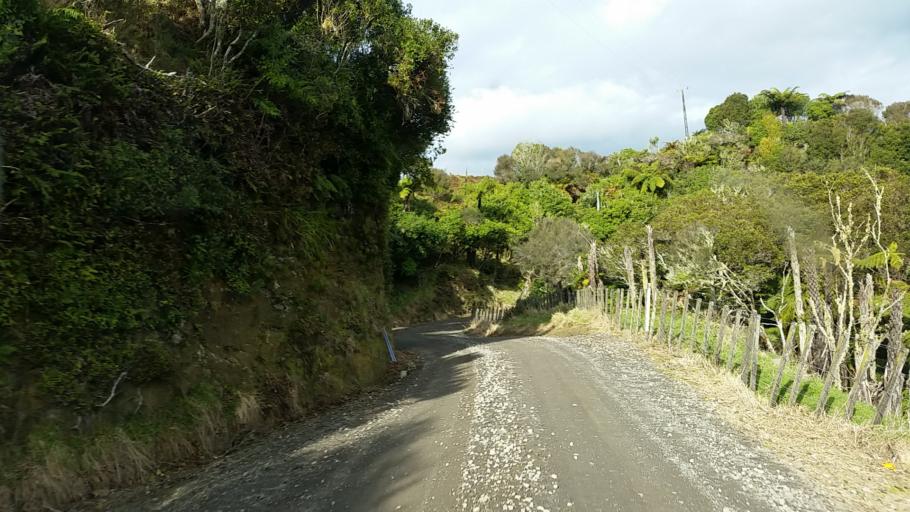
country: NZ
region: Taranaki
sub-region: South Taranaki District
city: Eltham
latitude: -39.1743
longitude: 174.6277
